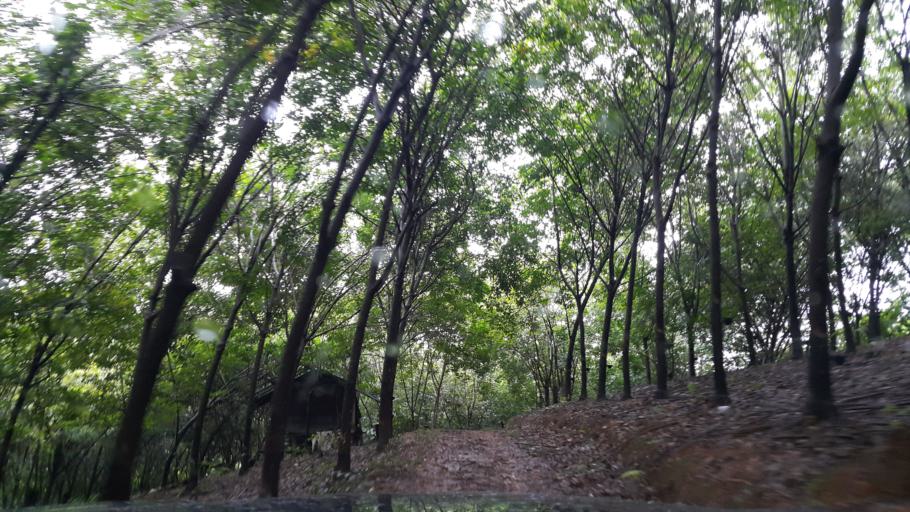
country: TH
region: Phayao
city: Phu Sang
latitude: 19.5973
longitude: 100.3995
